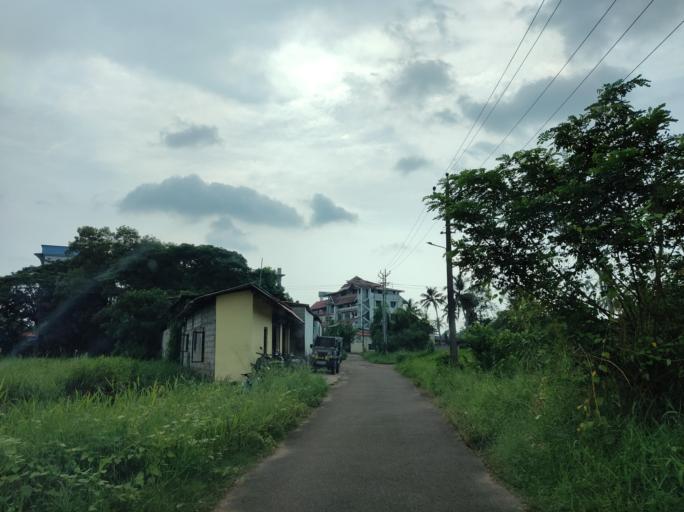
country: IN
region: Kerala
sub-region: Kottayam
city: Kottayam
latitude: 9.5733
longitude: 76.5212
